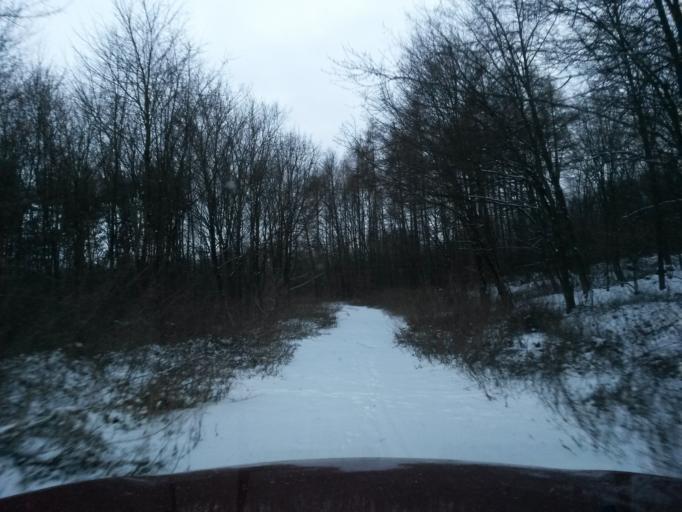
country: SK
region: Kosicky
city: Kosice
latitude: 48.7326
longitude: 21.3237
